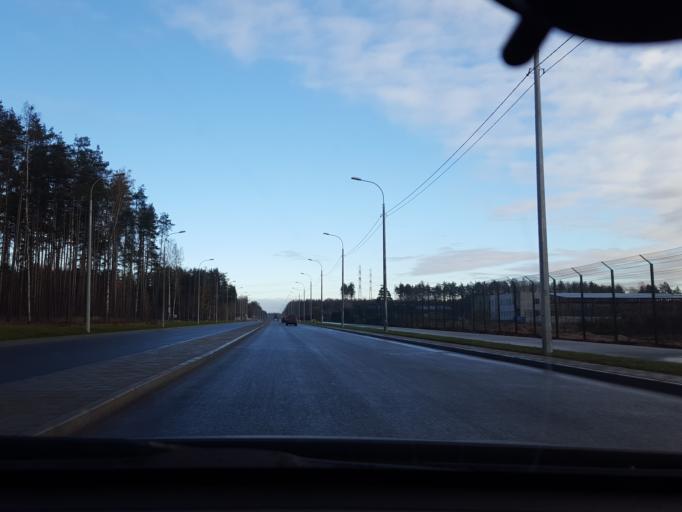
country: RU
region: Leningrad
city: Untolovo
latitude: 60.0537
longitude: 30.2298
